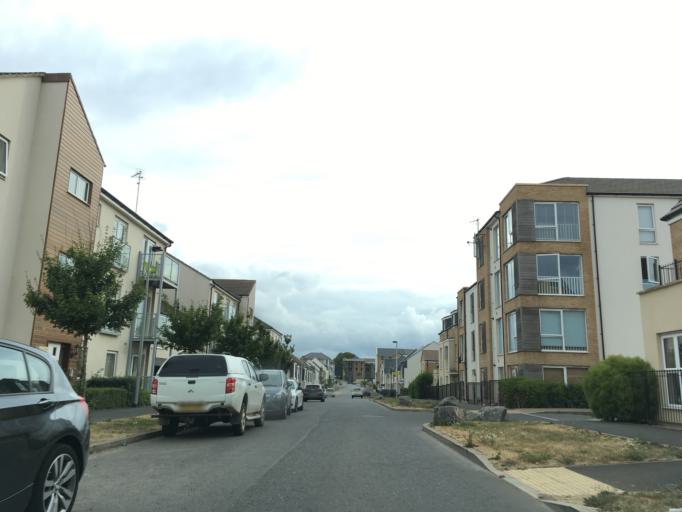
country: GB
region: England
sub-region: South Gloucestershire
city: Almondsbury
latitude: 51.5270
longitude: -2.5761
